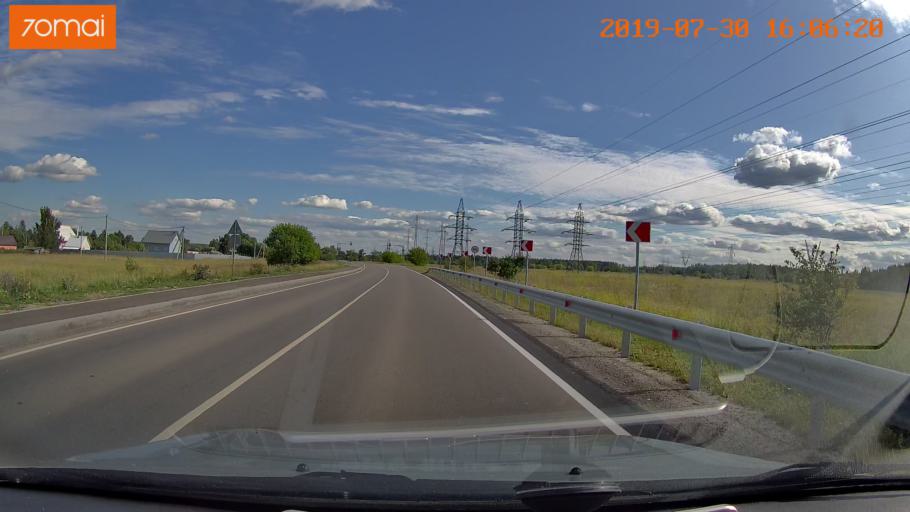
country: RU
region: Moskovskaya
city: Peski
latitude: 55.2568
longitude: 38.7160
